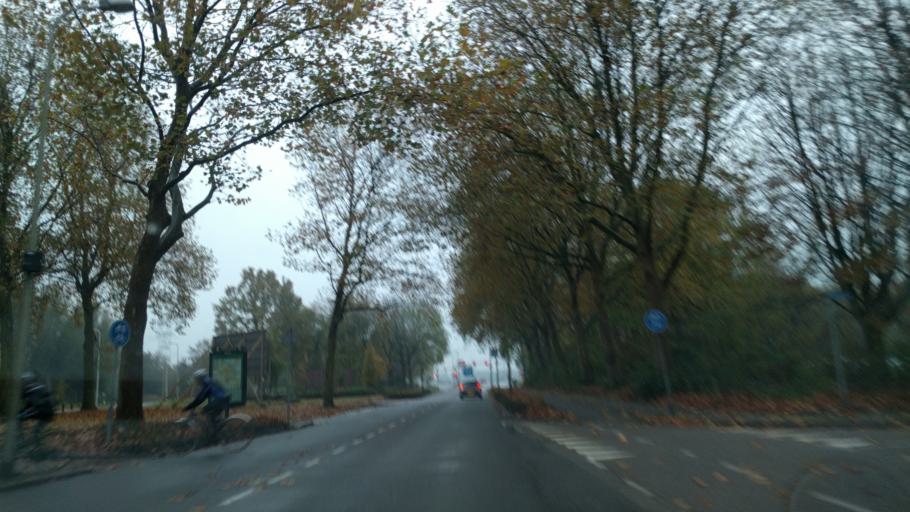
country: NL
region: South Holland
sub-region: Gemeente Ridderkerk
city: Ridderkerk
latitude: 51.8884
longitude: 4.5817
